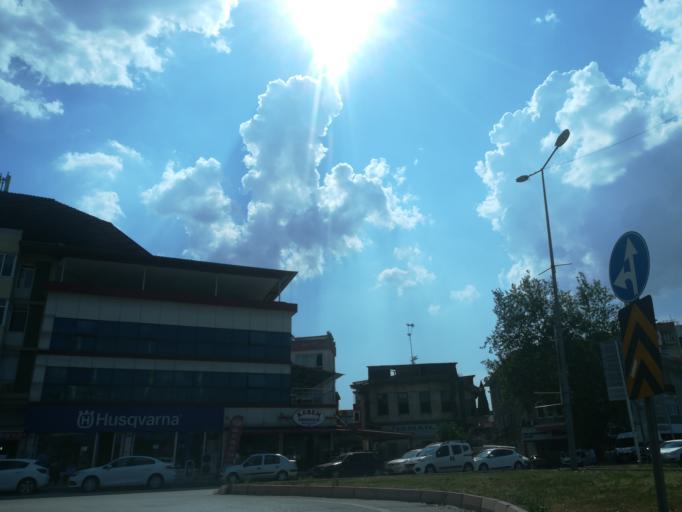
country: TR
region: Adana
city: Adana
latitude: 36.9894
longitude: 35.3316
